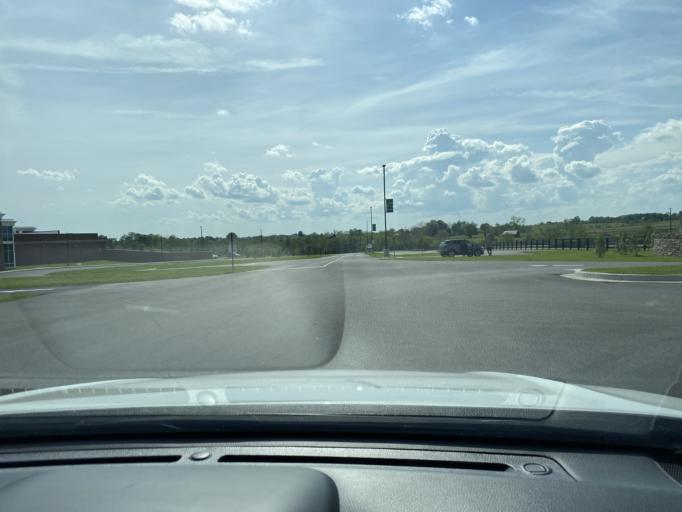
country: US
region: Kentucky
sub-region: Scott County
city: Georgetown
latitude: 38.2167
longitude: -84.5989
